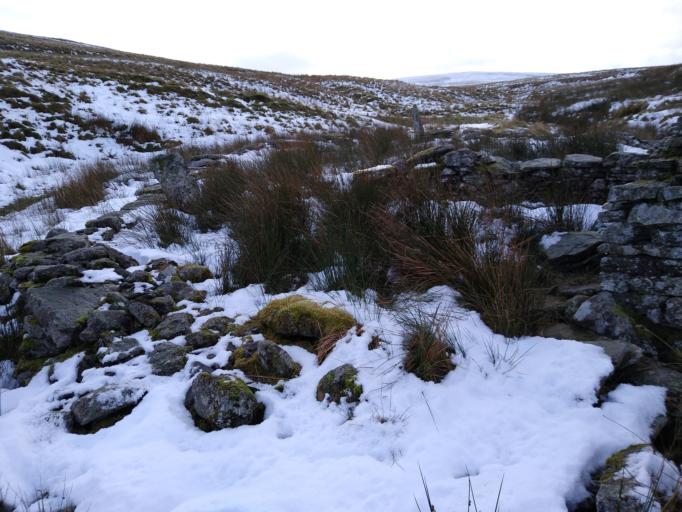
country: GB
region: England
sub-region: Cumbria
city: Penrith
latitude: 54.5722
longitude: -2.8417
